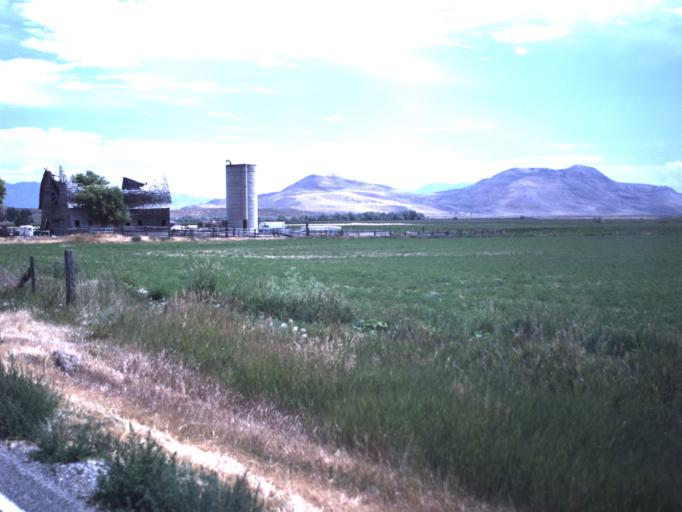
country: US
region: Utah
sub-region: Box Elder County
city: Tremonton
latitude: 41.6507
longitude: -112.3087
